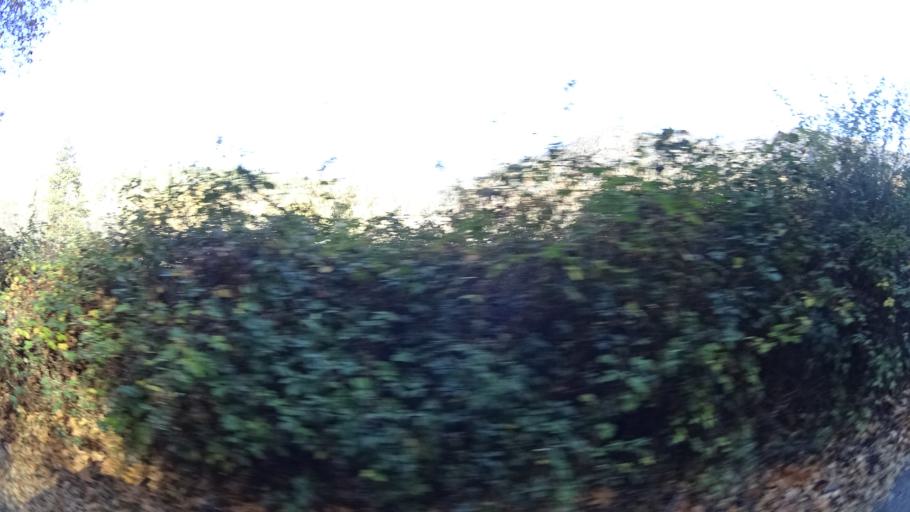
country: US
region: California
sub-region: Siskiyou County
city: Yreka
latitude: 41.8412
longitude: -122.8918
